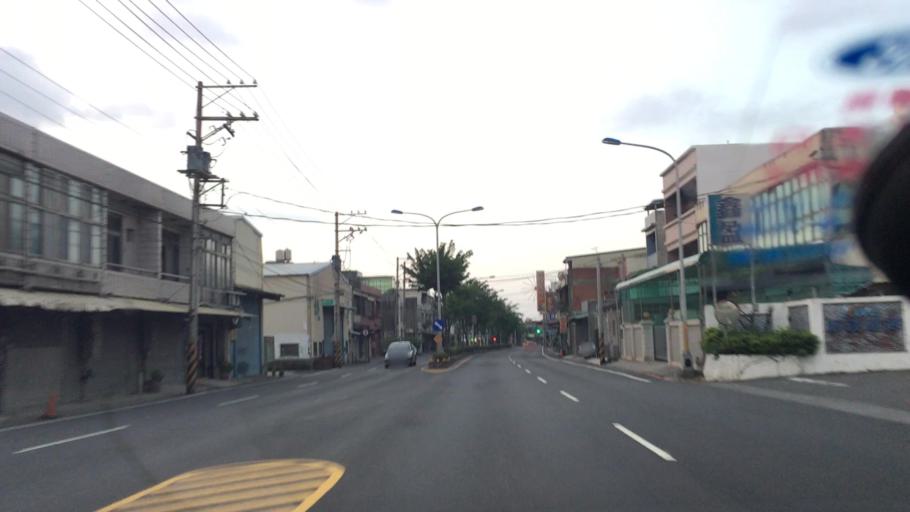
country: TW
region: Taiwan
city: Taoyuan City
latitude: 25.0593
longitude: 121.2675
